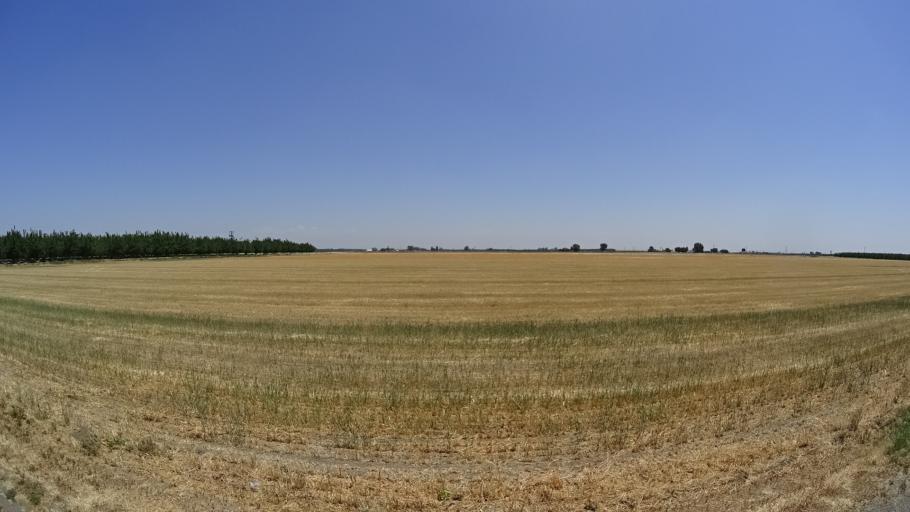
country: US
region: California
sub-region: Fresno County
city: Laton
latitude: 36.3896
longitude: -119.7371
